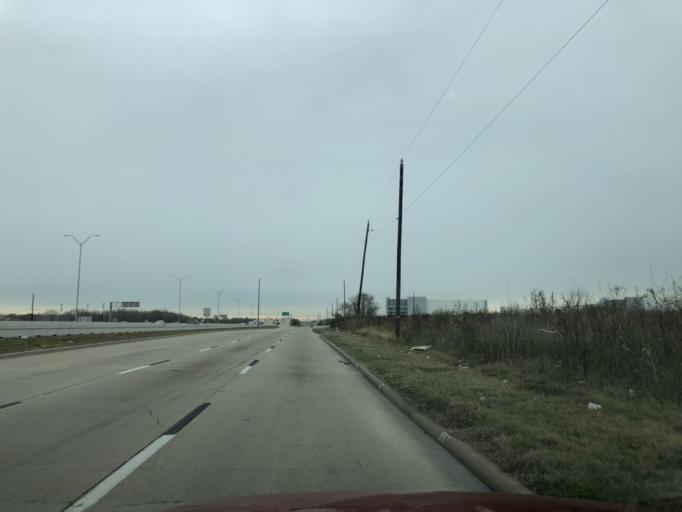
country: US
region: Texas
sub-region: Fort Bend County
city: Missouri City
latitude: 29.6325
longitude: -95.5258
